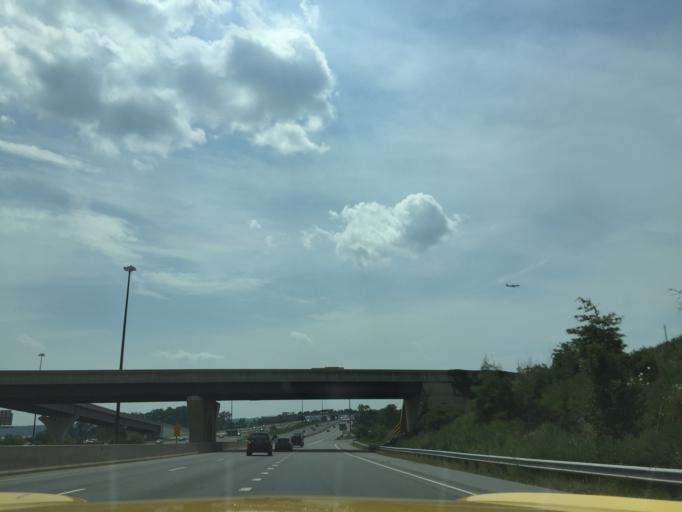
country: US
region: Maryland
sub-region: Prince George's County
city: Forest Heights
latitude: 38.7954
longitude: -77.0159
